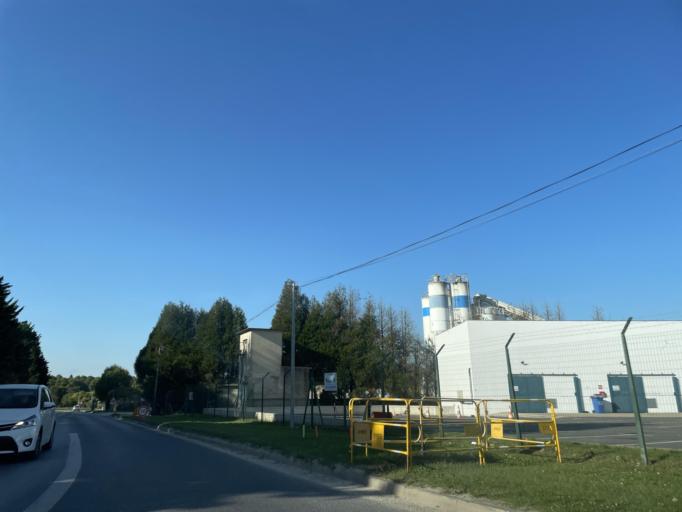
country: FR
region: Ile-de-France
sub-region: Departement de Seine-et-Marne
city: Coulommiers
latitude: 48.8067
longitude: 3.0939
